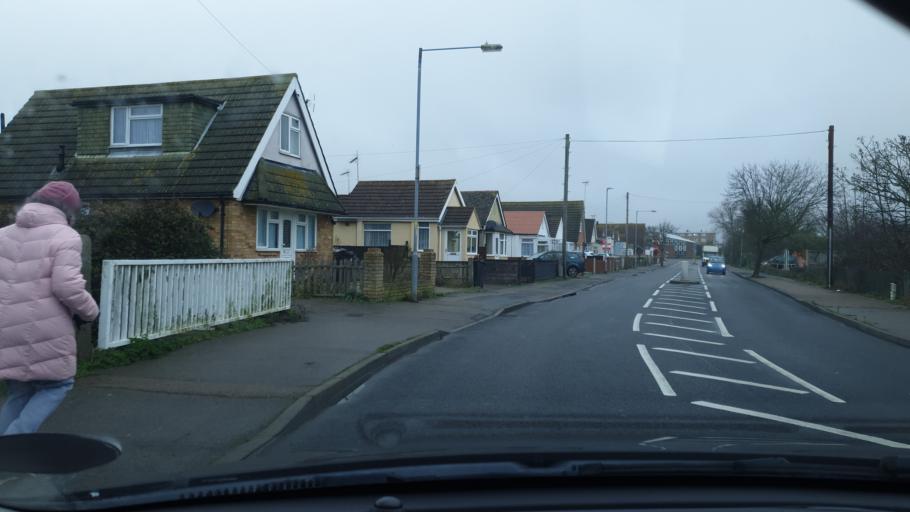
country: GB
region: England
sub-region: Essex
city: Clacton-on-Sea
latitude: 51.7797
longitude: 1.1204
